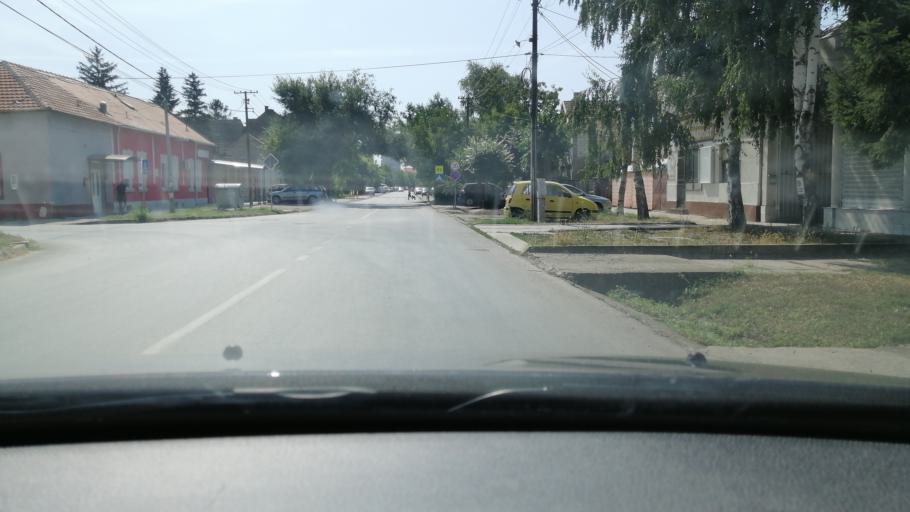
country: RS
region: Autonomna Pokrajina Vojvodina
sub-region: Srednjebanatski Okrug
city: Zrenjanin
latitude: 45.3870
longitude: 20.3858
